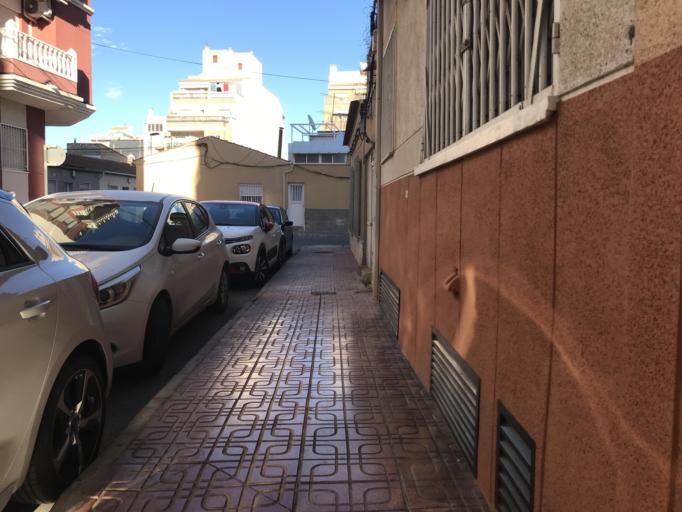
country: ES
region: Valencia
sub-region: Provincia de Alicante
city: Torrevieja
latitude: 37.9815
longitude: -0.6839
